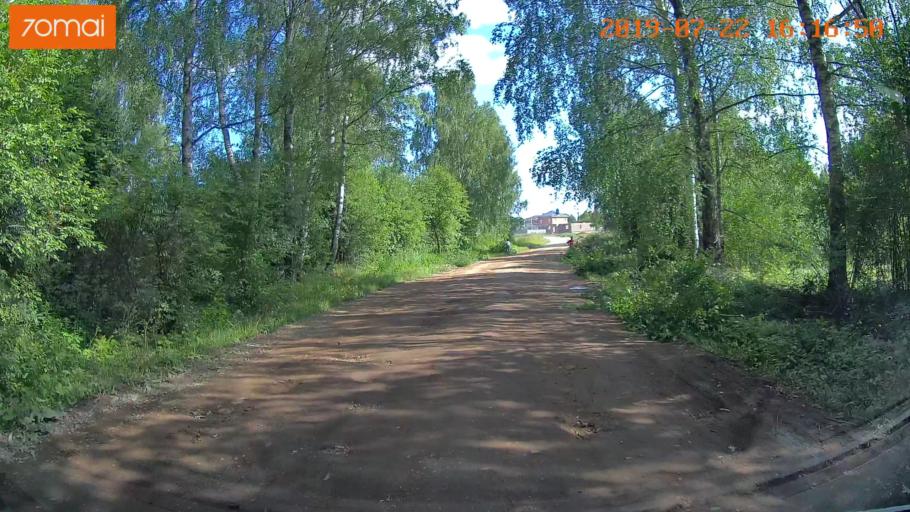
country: RU
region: Ivanovo
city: Novo-Talitsy
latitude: 57.0707
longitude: 40.8822
